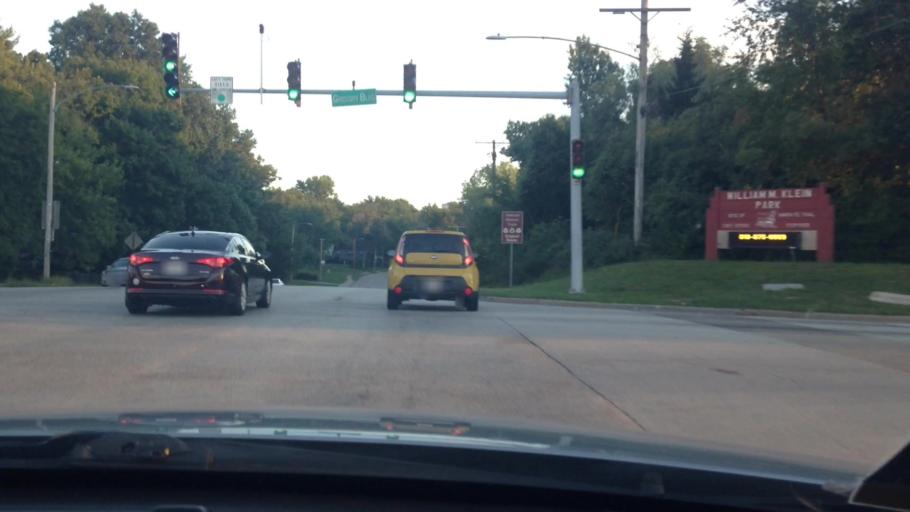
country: US
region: Missouri
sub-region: Jackson County
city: Raytown
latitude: 38.9953
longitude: -94.4825
